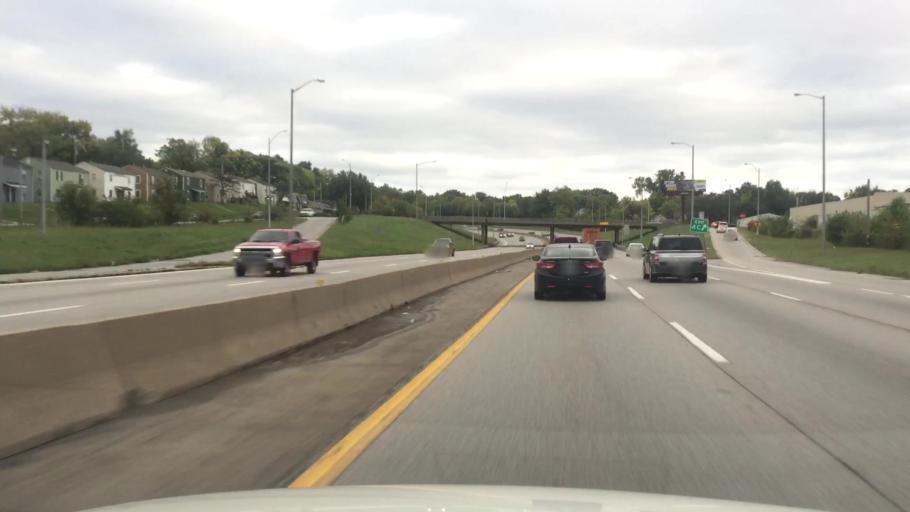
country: US
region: Missouri
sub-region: Jackson County
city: Kansas City
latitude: 39.0863
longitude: -94.5412
